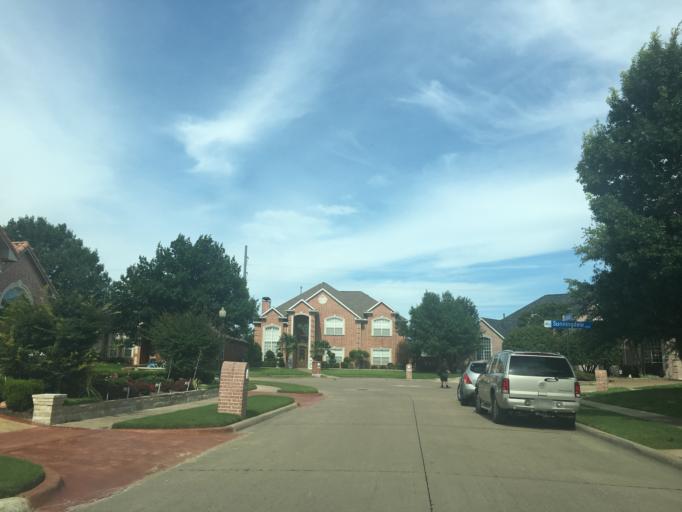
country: US
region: Texas
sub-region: Dallas County
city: Richardson
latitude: 32.9318
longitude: -96.7146
